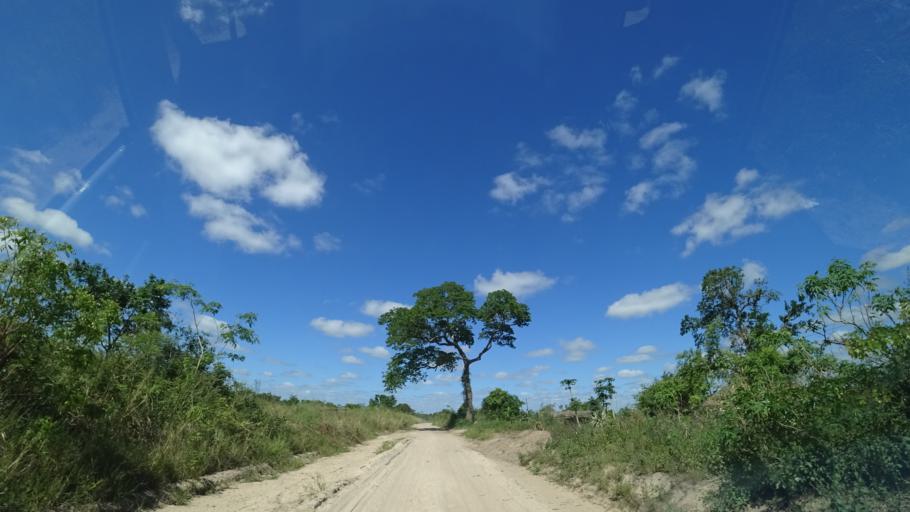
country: MZ
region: Sofala
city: Dondo
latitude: -19.2911
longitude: 34.6891
